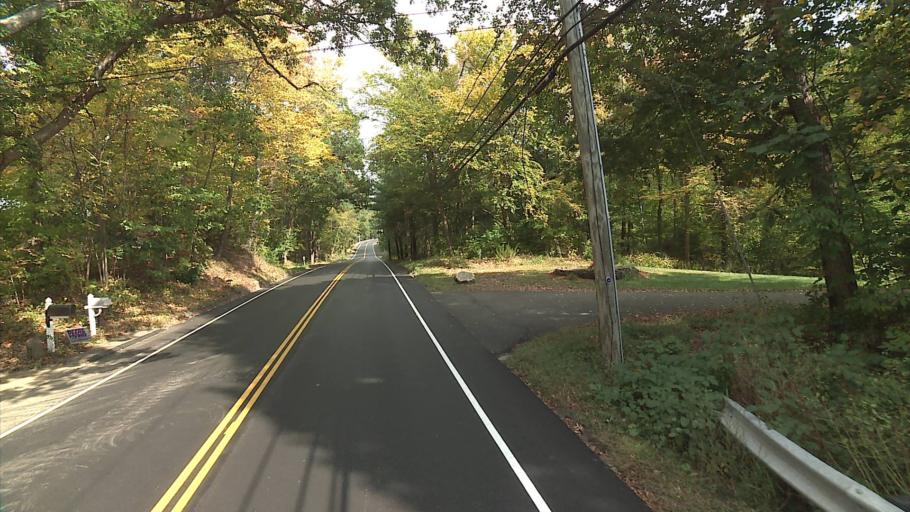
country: US
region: Connecticut
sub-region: Litchfield County
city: Watertown
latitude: 41.6161
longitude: -73.1109
